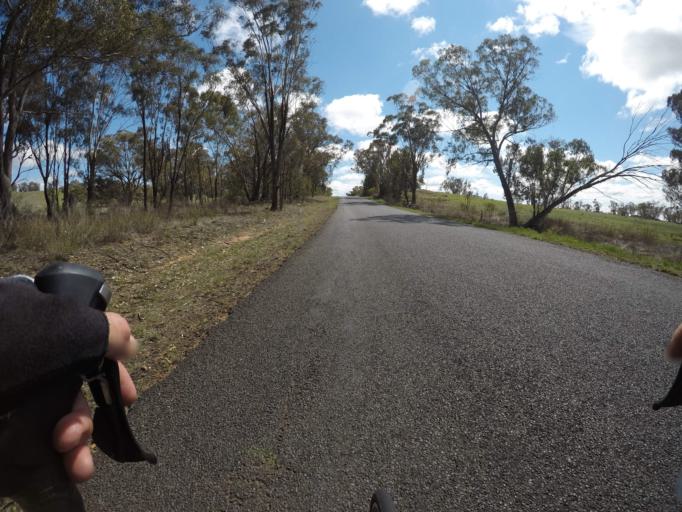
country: AU
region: New South Wales
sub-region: Dubbo Municipality
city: Dubbo
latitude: -32.5202
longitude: 148.5544
